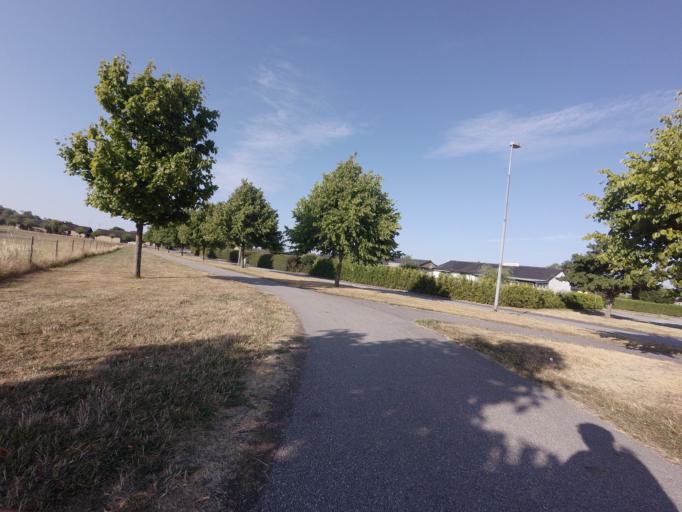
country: SE
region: Skane
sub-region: Trelleborgs Kommun
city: Trelleborg
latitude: 55.3617
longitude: 13.2261
